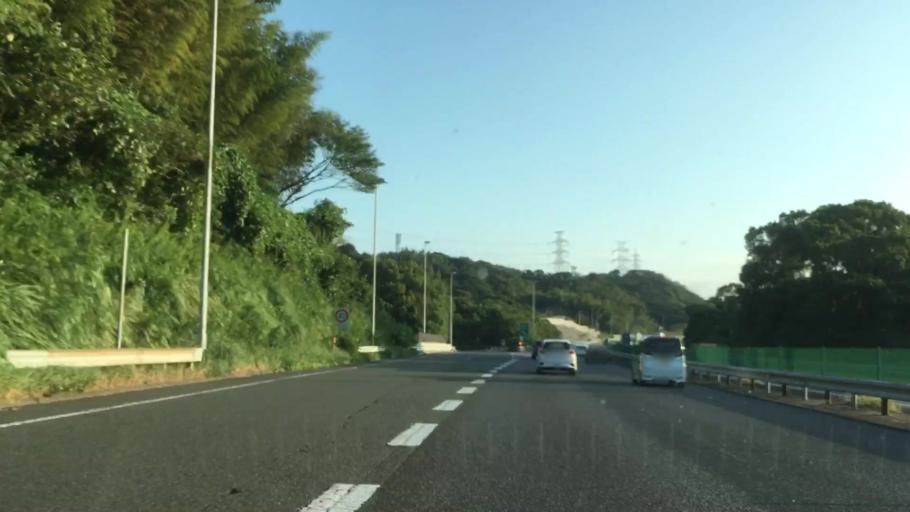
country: JP
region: Yamaguchi
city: Shimonoseki
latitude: 33.9796
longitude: 130.9526
